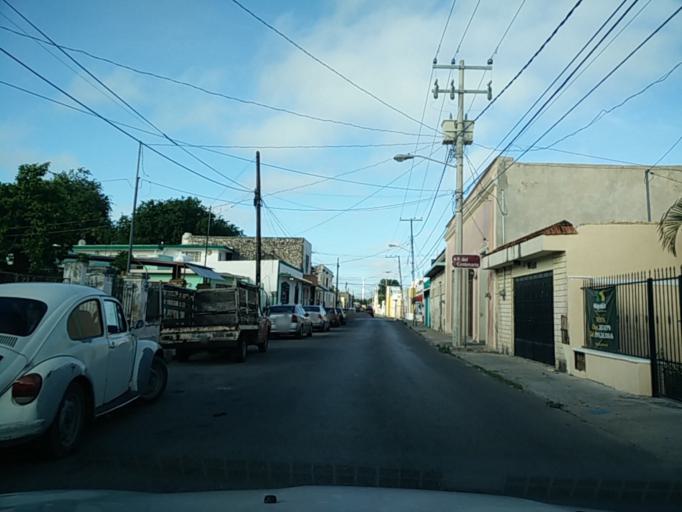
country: MX
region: Yucatan
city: Merida
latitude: 20.9673
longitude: -89.6361
